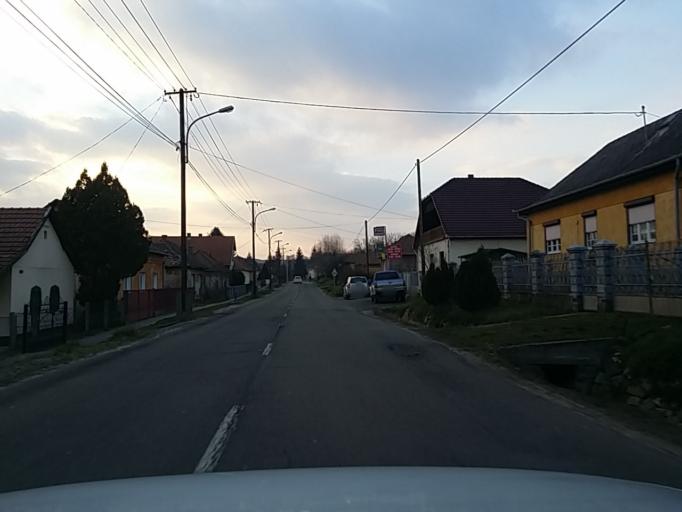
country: HU
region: Nograd
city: Matraterenye
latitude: 48.0040
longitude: 19.9102
